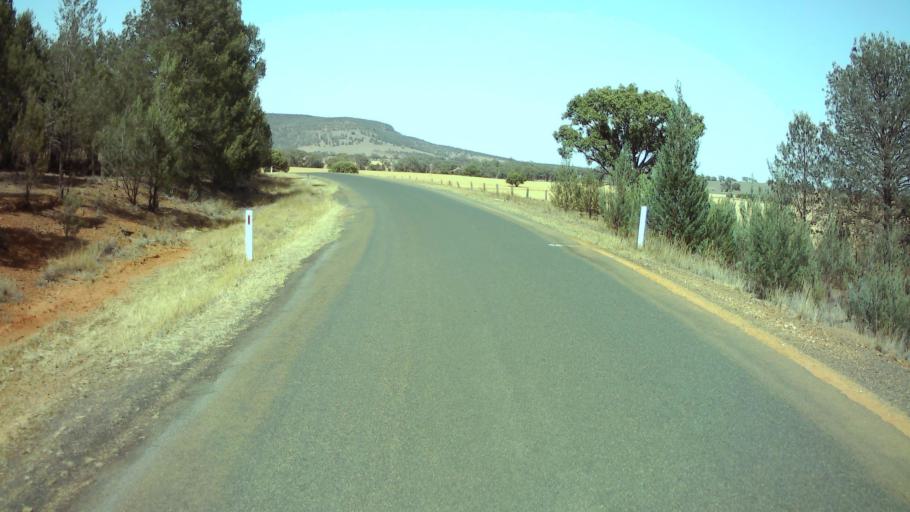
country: AU
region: New South Wales
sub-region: Weddin
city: Grenfell
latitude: -33.8616
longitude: 148.0143
